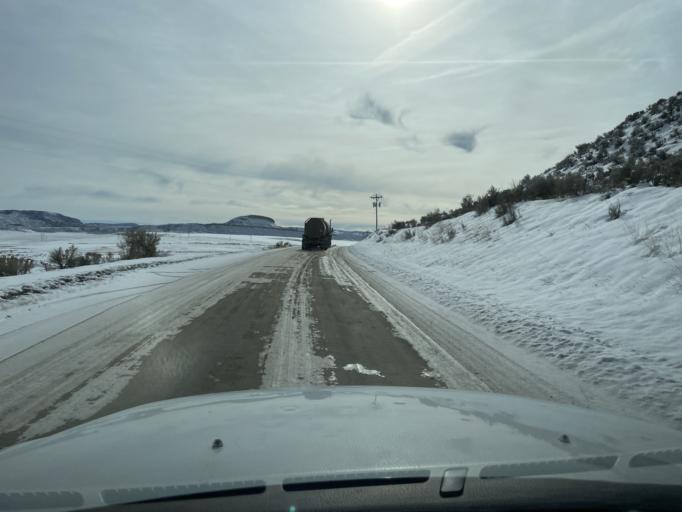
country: US
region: Colorado
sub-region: Moffat County
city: Craig
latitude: 40.3324
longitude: -107.6879
